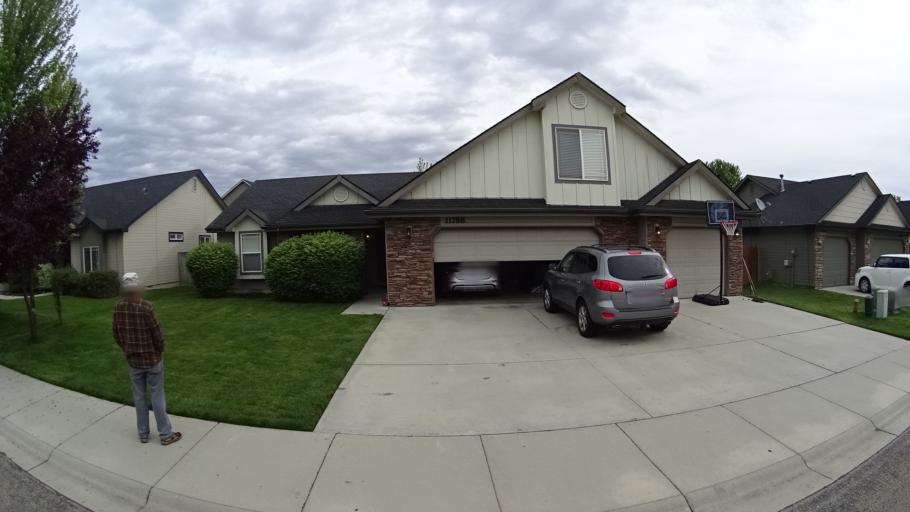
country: US
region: Idaho
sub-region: Ada County
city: Star
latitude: 43.6961
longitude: -116.5003
